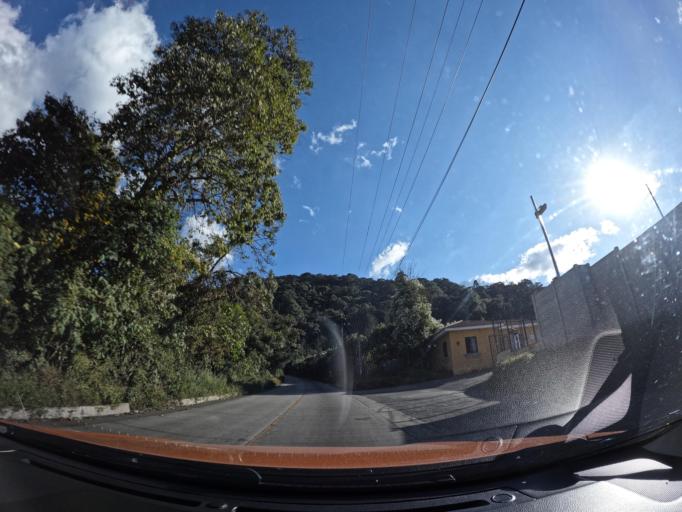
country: GT
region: Sacatepequez
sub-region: Municipio de Santa Maria de Jesus
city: Santa Maria de Jesus
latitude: 14.5140
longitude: -90.7221
